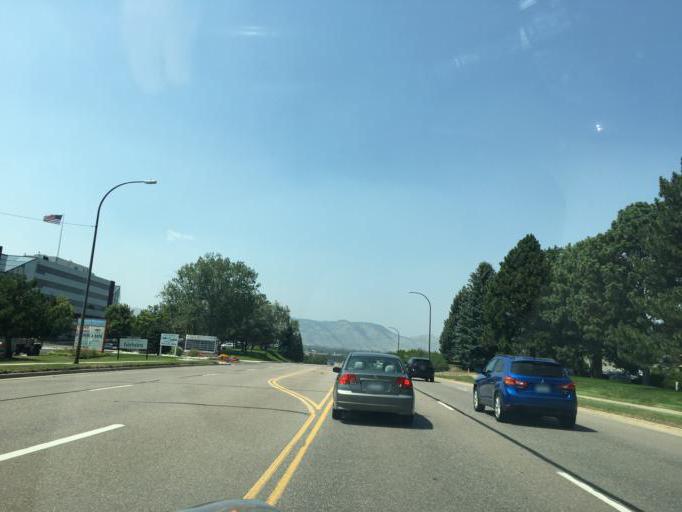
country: US
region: Colorado
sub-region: Jefferson County
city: Applewood
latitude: 39.7401
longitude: -105.1385
